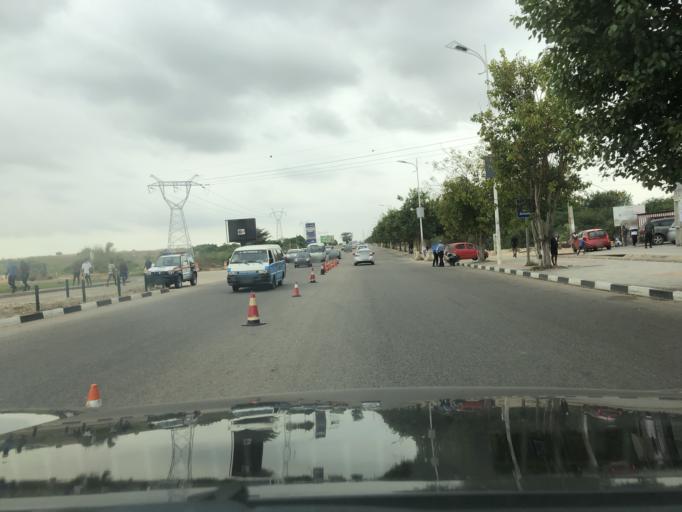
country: AO
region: Luanda
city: Luanda
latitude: -8.9883
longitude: 13.2905
